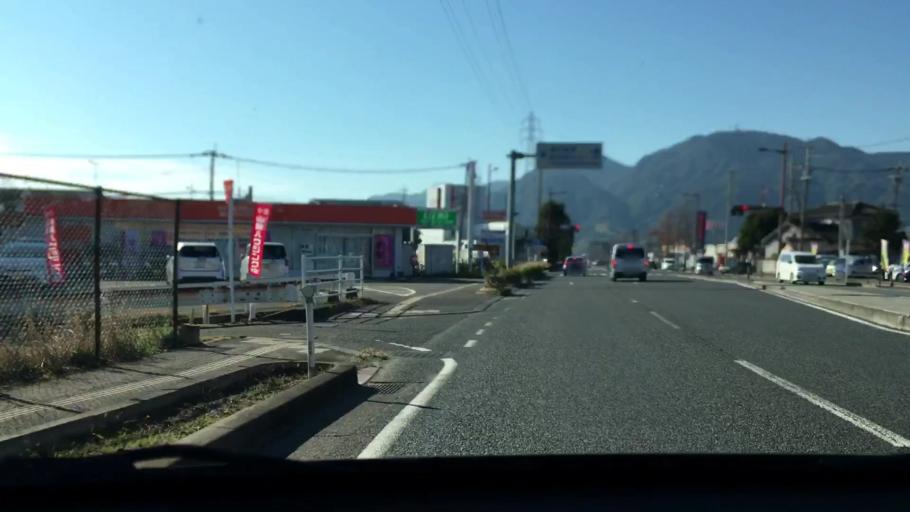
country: JP
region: Kagoshima
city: Kajiki
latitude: 31.7232
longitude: 130.6227
